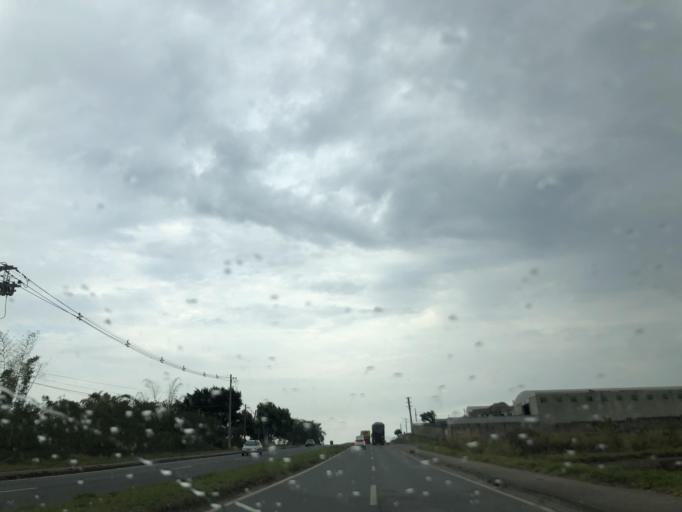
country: BR
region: Sao Paulo
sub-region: Salto De Pirapora
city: Salto de Pirapora
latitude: -23.6416
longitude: -47.5806
